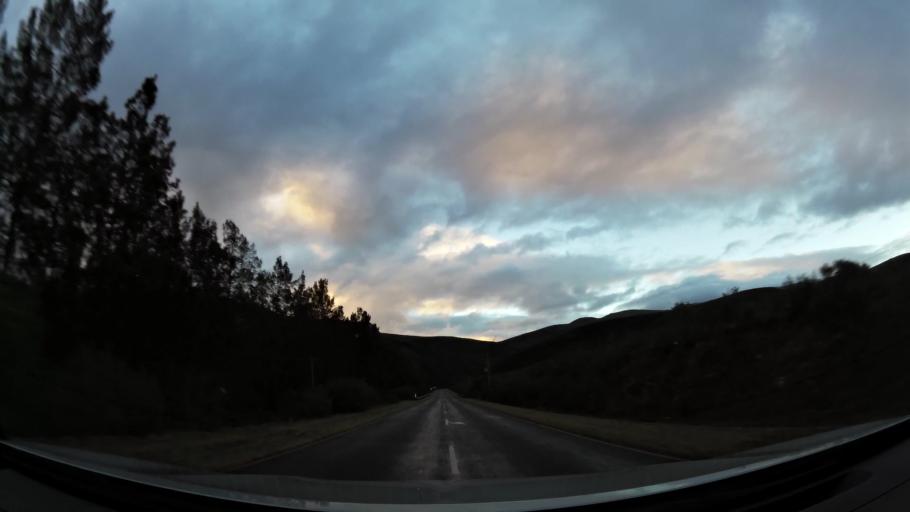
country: ZA
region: Western Cape
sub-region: Overberg District Municipality
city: Swellendam
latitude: -34.0008
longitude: 20.7053
